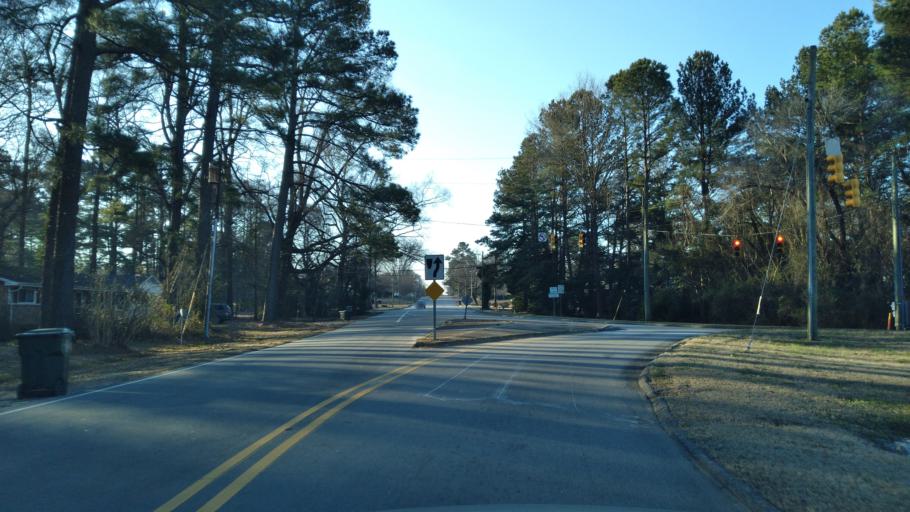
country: US
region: North Carolina
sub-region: Wake County
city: Garner
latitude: 35.7048
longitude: -78.6191
